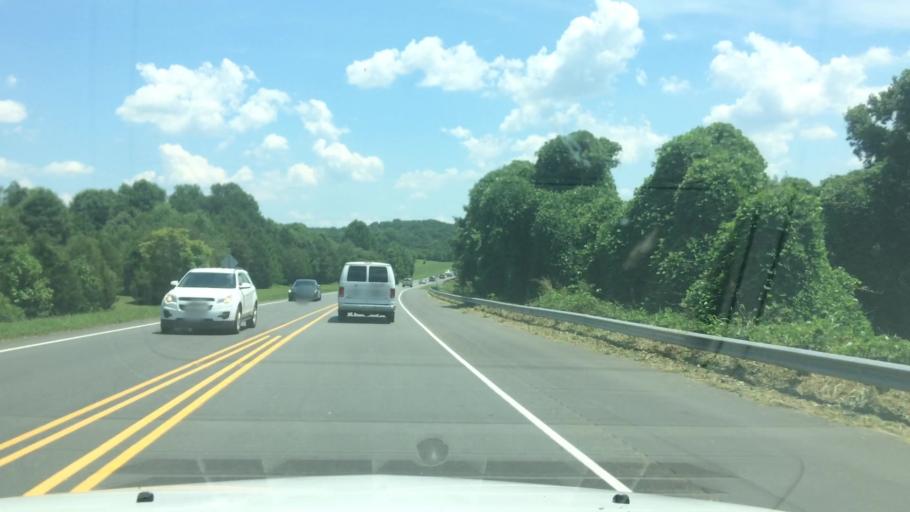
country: US
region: North Carolina
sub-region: Alexander County
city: Stony Point
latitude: 35.8144
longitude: -80.9818
